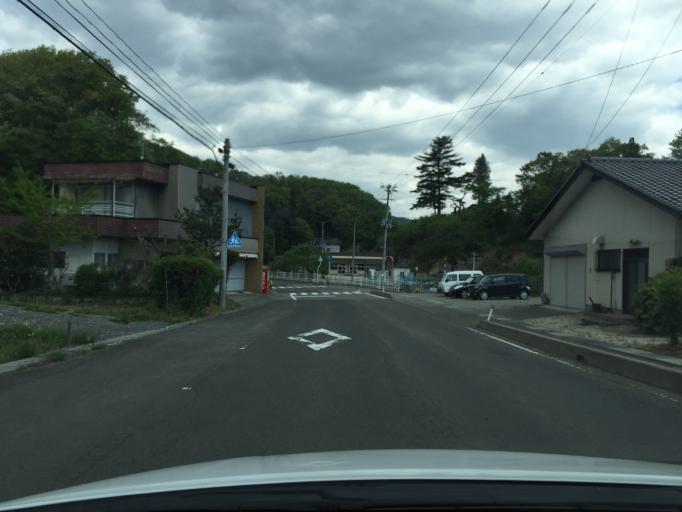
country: JP
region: Fukushima
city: Fukushima-shi
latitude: 37.6841
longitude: 140.5613
